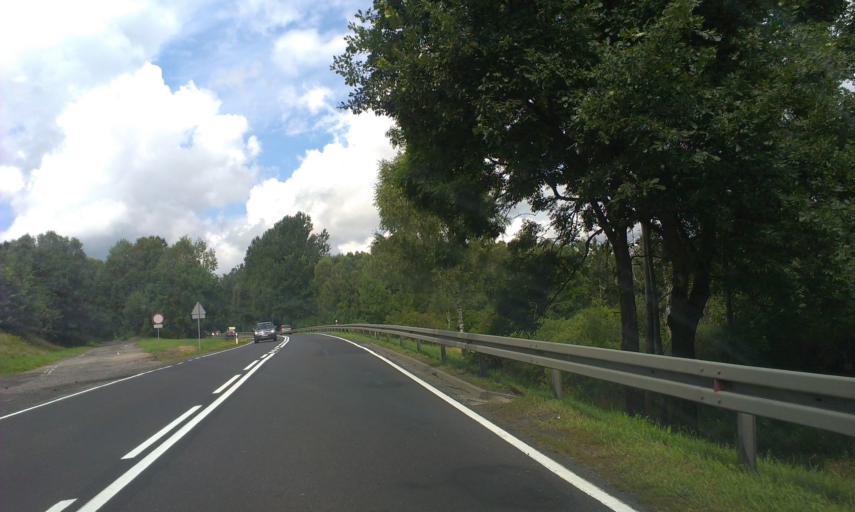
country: PL
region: West Pomeranian Voivodeship
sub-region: Powiat koszalinski
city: Bobolice
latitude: 53.9665
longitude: 16.5712
